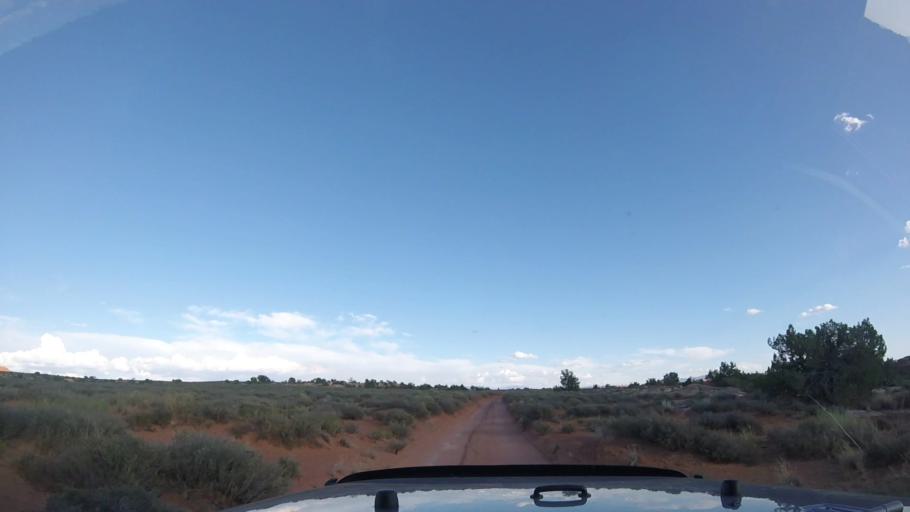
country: US
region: Utah
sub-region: Grand County
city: Moab
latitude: 38.2028
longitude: -109.7837
